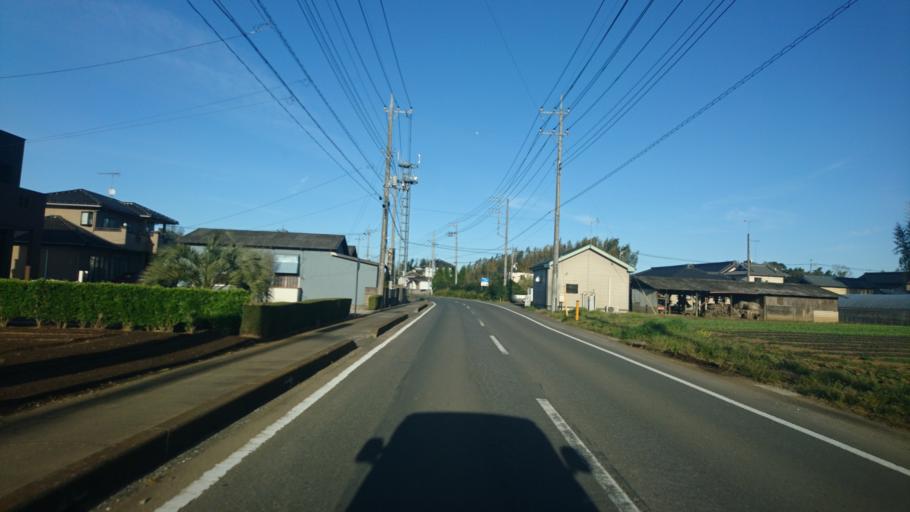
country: JP
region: Ibaraki
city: Shimodate
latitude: 36.2513
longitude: 139.9380
